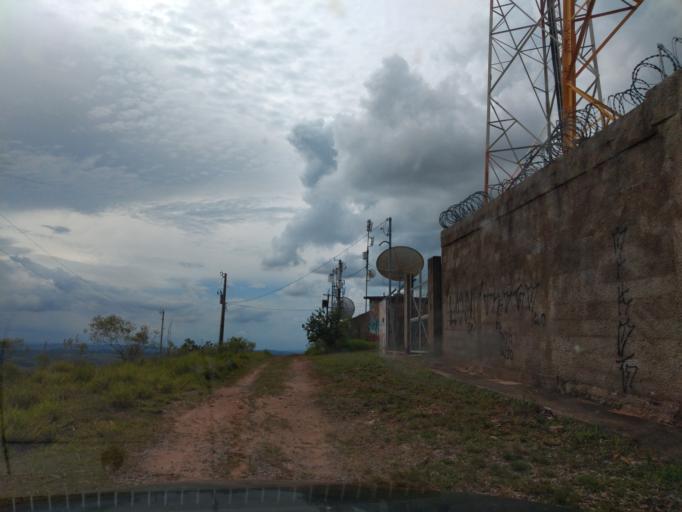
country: BR
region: Minas Gerais
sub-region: Lavras
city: Lavras
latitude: -21.5274
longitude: -44.9037
